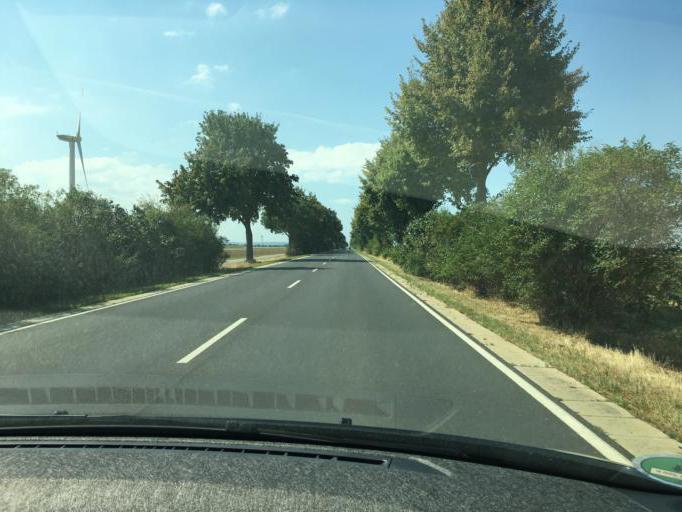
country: DE
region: North Rhine-Westphalia
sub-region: Regierungsbezirk Koln
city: Merzenich
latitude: 50.8309
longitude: 6.5641
